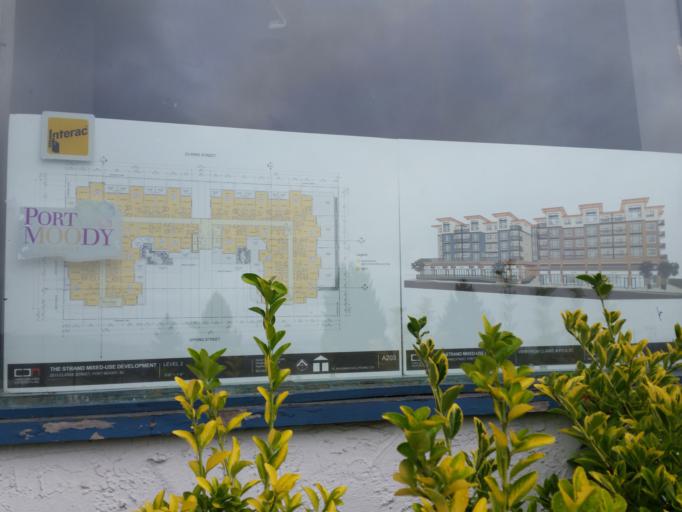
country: CA
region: British Columbia
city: Port Moody
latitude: 49.2776
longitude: -122.8557
